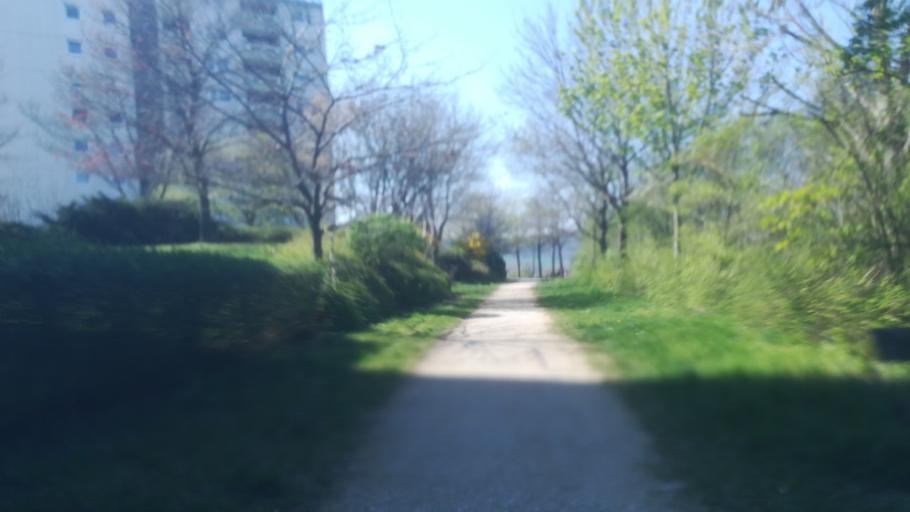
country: DE
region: Baden-Wuerttemberg
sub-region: Freiburg Region
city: Singen
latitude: 47.7793
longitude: 8.8565
